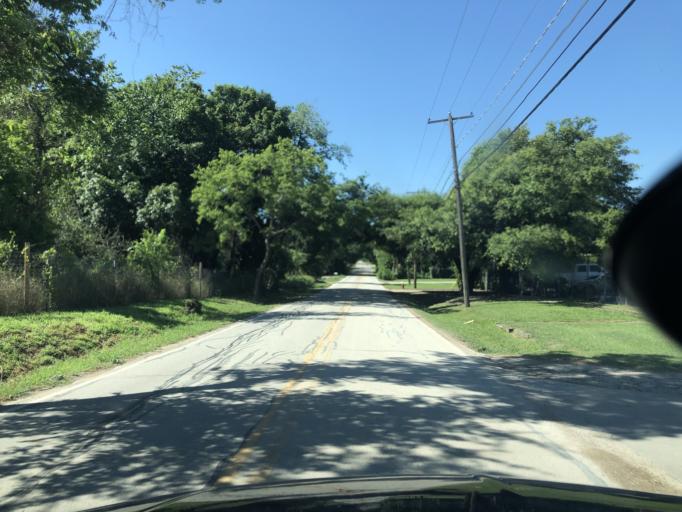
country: US
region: Texas
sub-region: Dallas County
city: Grand Prairie
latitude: 32.8066
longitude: -97.0204
